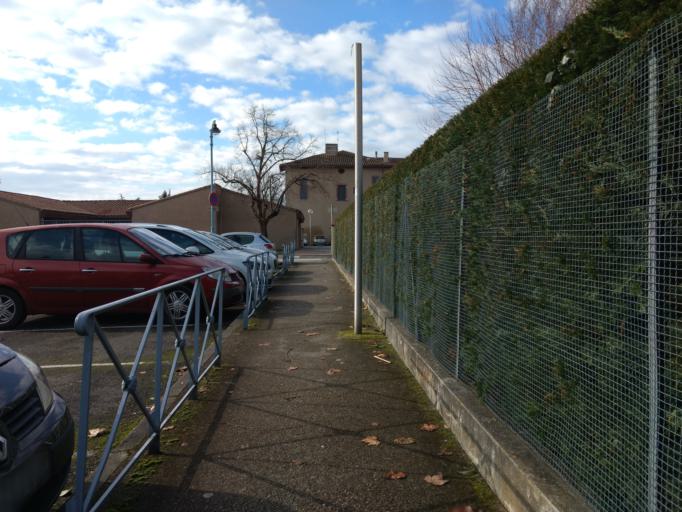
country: FR
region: Midi-Pyrenees
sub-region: Departement de la Haute-Garonne
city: Tournefeuille
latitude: 43.5834
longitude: 1.3474
